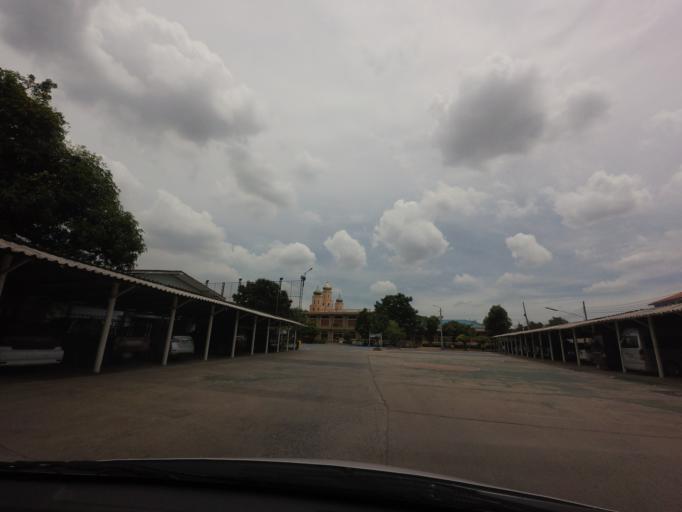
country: TH
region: Nonthaburi
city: Mueang Nonthaburi
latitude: 13.8888
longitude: 100.5199
